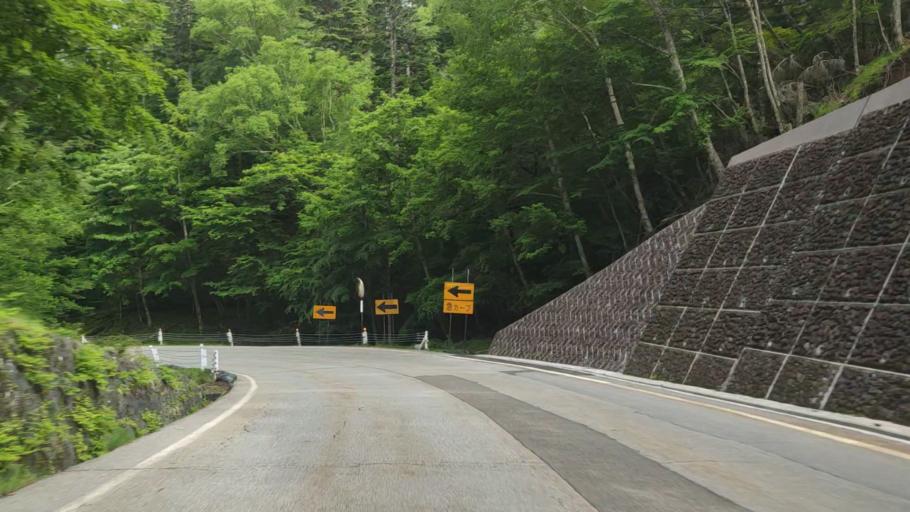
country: JP
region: Yamanashi
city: Fujikawaguchiko
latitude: 35.4151
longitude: 138.7135
